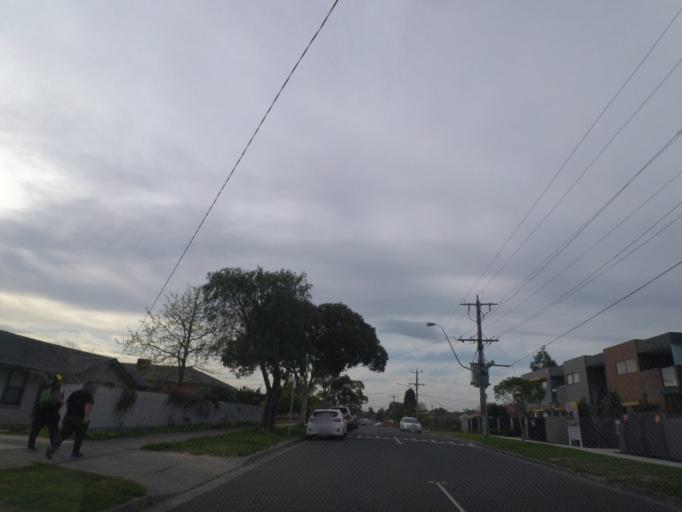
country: AU
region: Victoria
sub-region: Knox
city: Ferntree Gully
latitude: -37.8858
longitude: 145.2761
